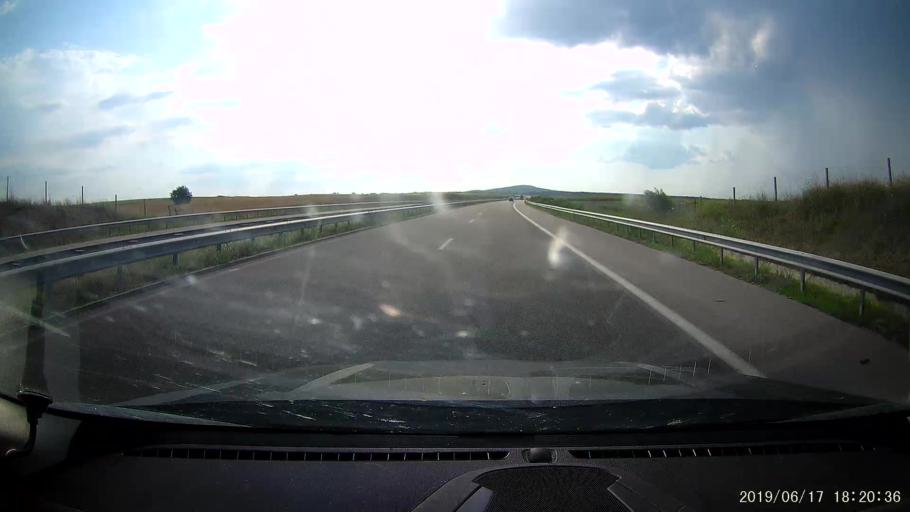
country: BG
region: Khaskovo
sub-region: Obshtina Simeonovgrad
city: Simeonovgrad
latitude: 41.9627
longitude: 25.8080
